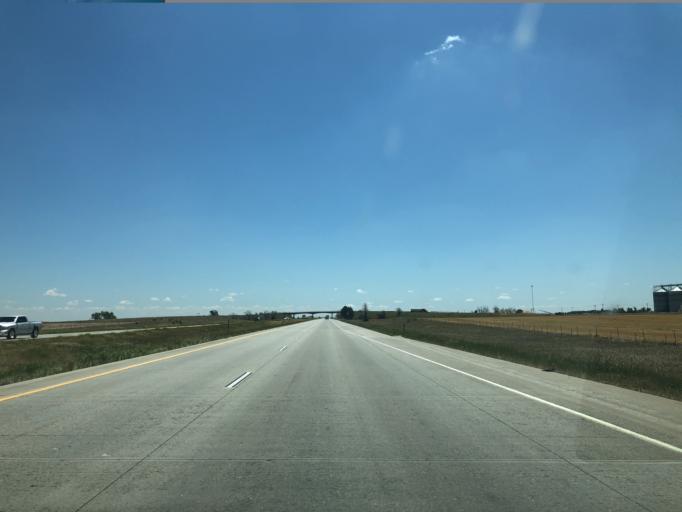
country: US
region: Colorado
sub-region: Arapahoe County
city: Byers
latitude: 39.7133
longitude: -104.2153
